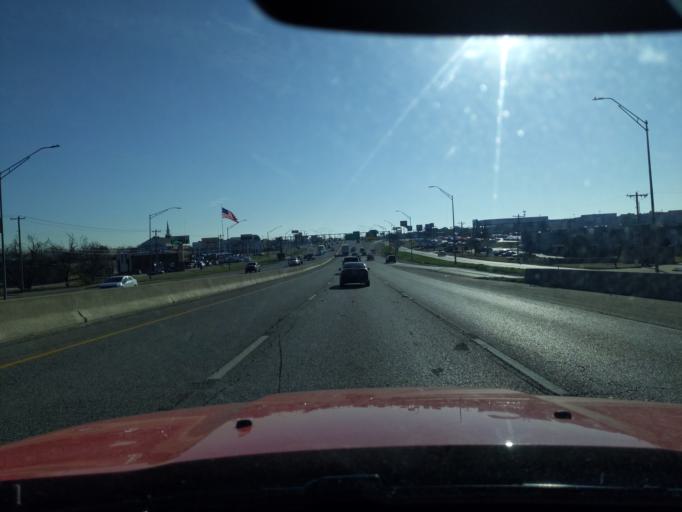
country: US
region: Oklahoma
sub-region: Cleveland County
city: Moore
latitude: 35.3913
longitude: -97.5279
